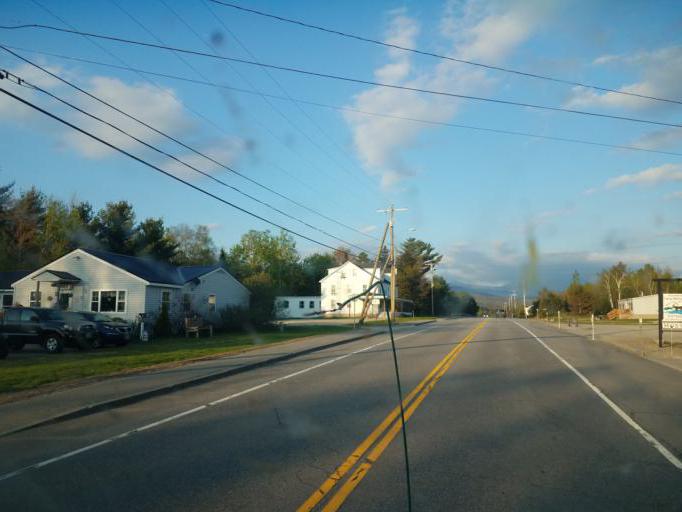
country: US
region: New Hampshire
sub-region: Grafton County
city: Deerfield
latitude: 44.2677
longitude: -71.5527
